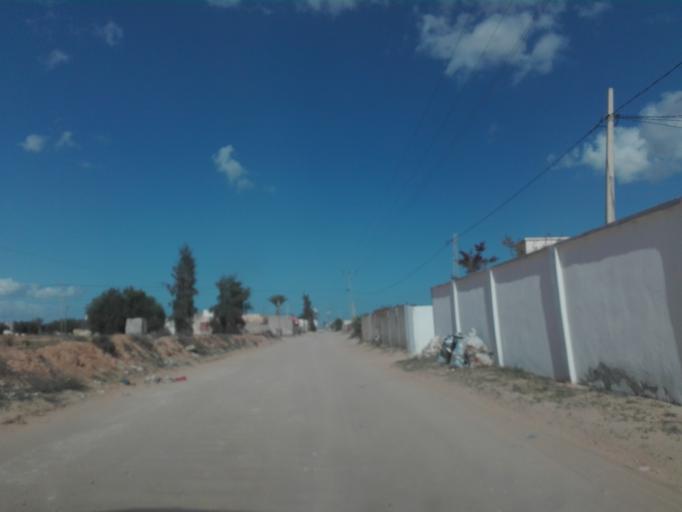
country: TN
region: Madanin
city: Bin Qirdan
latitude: 33.1549
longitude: 11.1936
